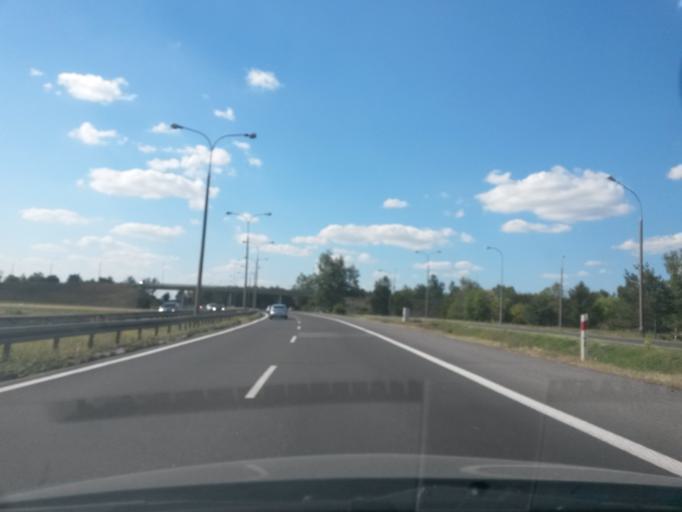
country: PL
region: Masovian Voivodeship
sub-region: Powiat nowodworski
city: Zakroczym
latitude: 52.4394
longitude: 20.6447
